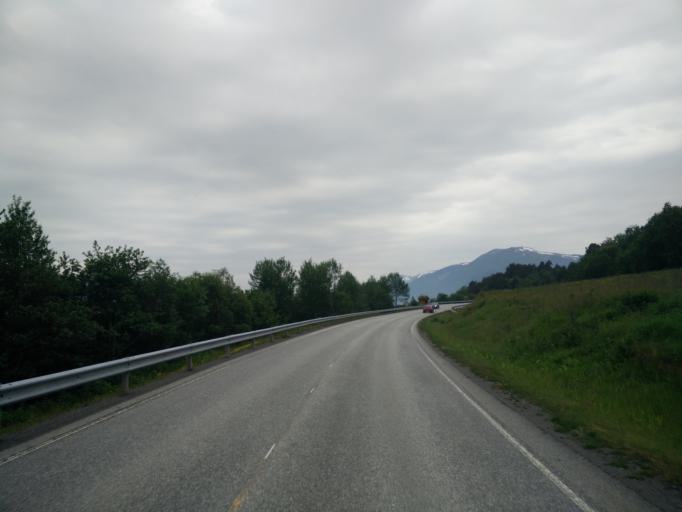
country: NO
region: More og Romsdal
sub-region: Kristiansund
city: Rensvik
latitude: 62.9772
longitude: 7.8620
